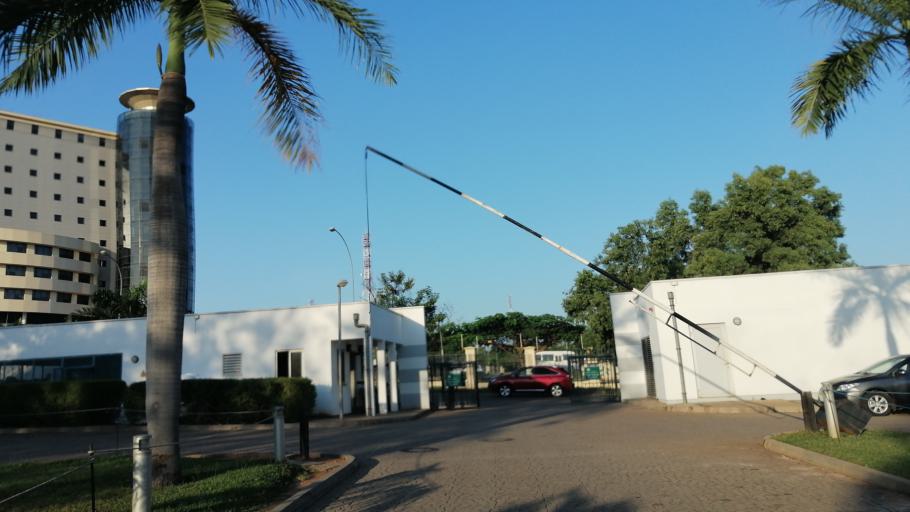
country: NG
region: Abuja Federal Capital Territory
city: Abuja
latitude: 9.0647
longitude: 7.4866
